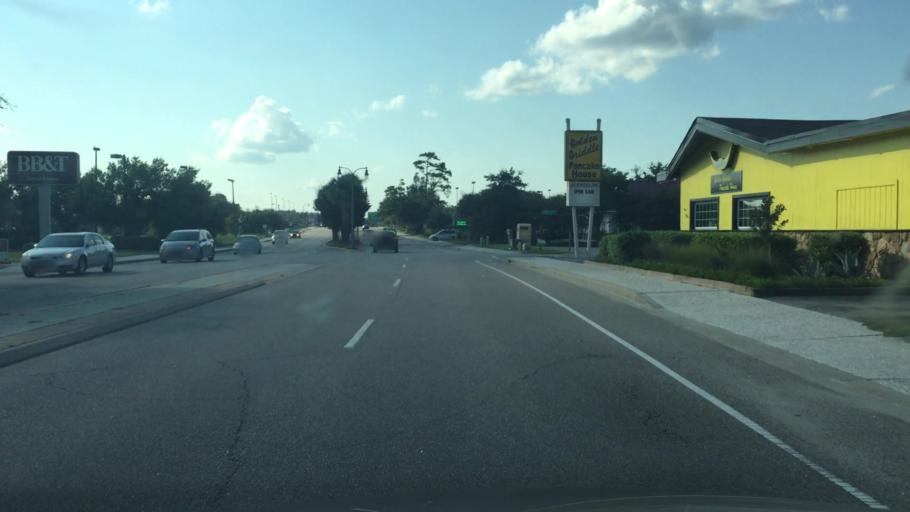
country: US
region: South Carolina
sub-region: Horry County
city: North Myrtle Beach
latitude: 33.8245
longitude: -78.6756
